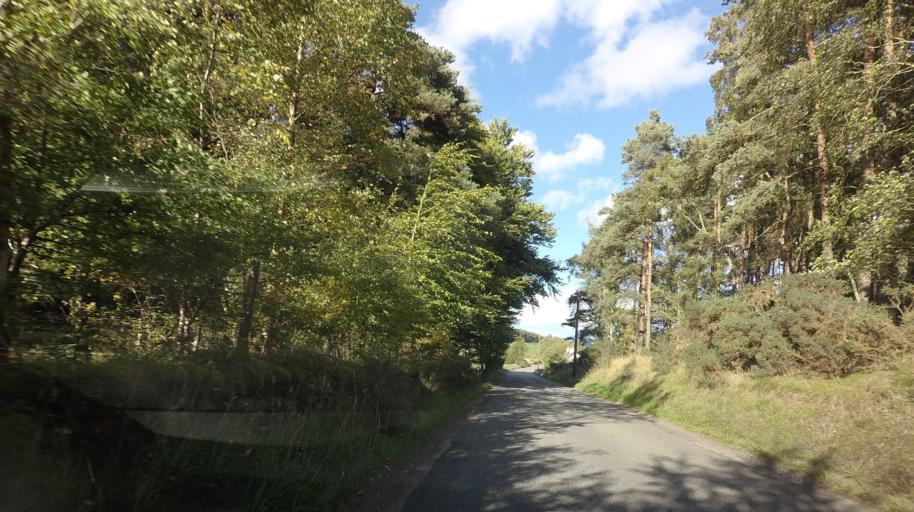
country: GB
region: Scotland
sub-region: Aberdeenshire
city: Banchory
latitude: 57.0739
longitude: -2.4634
